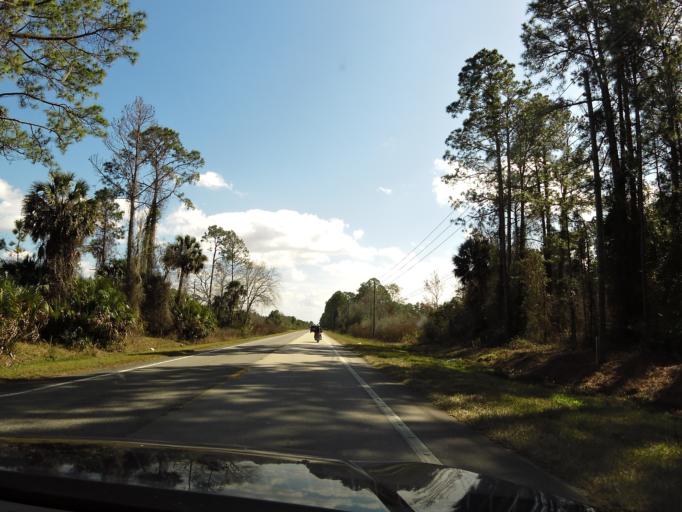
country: US
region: Florida
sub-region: Volusia County
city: De Leon Springs
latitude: 29.1768
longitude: -81.4077
